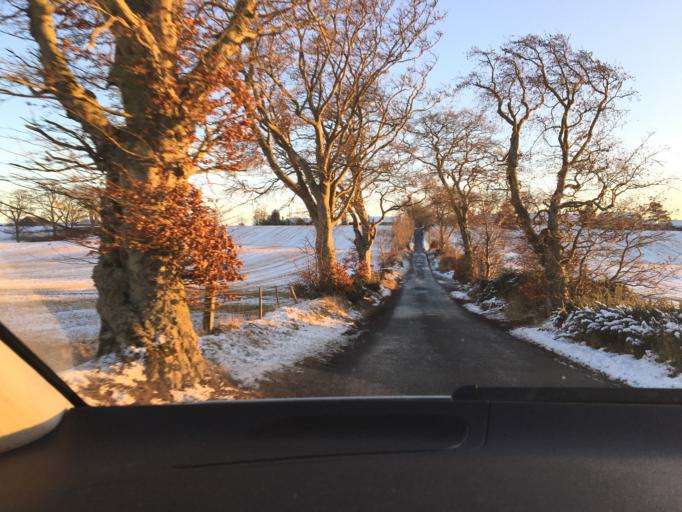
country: GB
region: Scotland
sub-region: The Scottish Borders
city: Saint Boswells
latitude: 55.5974
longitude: -2.6442
